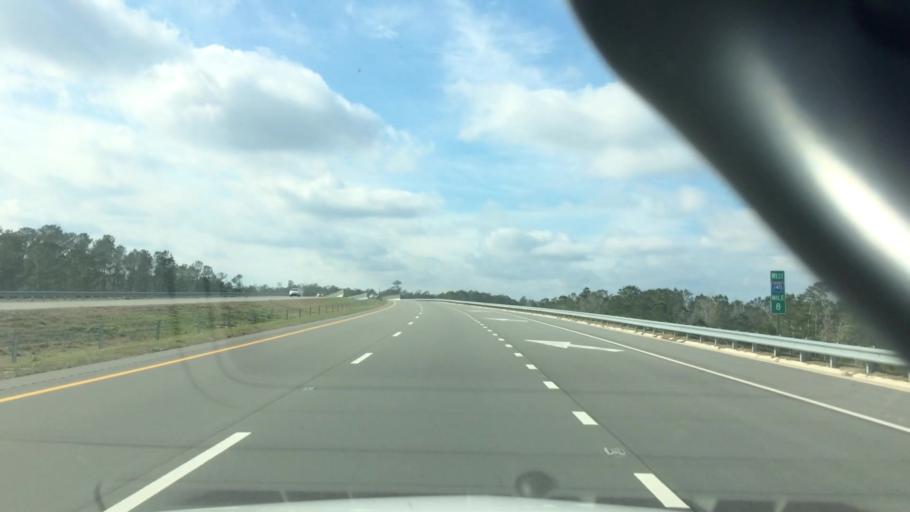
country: US
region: North Carolina
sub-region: Brunswick County
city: Leland
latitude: 34.2796
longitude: -78.0566
